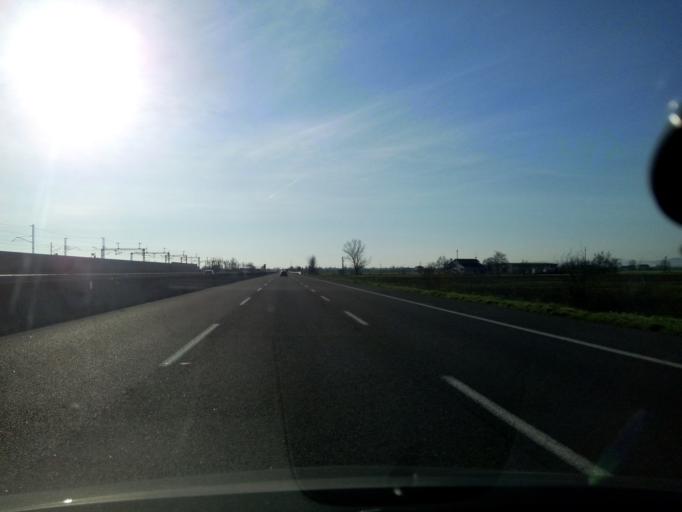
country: IT
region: Emilia-Romagna
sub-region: Provincia di Reggio Emilia
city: Campegine
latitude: 44.7548
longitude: 10.5474
